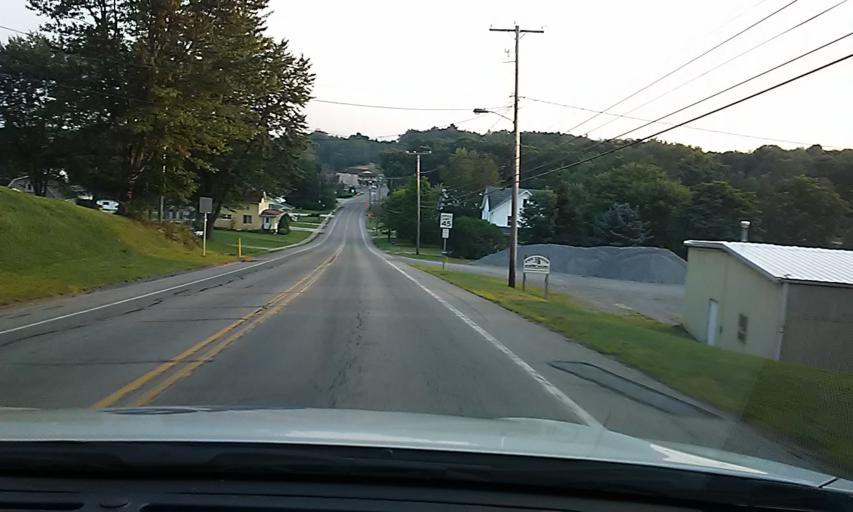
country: US
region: Pennsylvania
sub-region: Clarion County
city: Marianne
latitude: 41.3107
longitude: -79.3674
